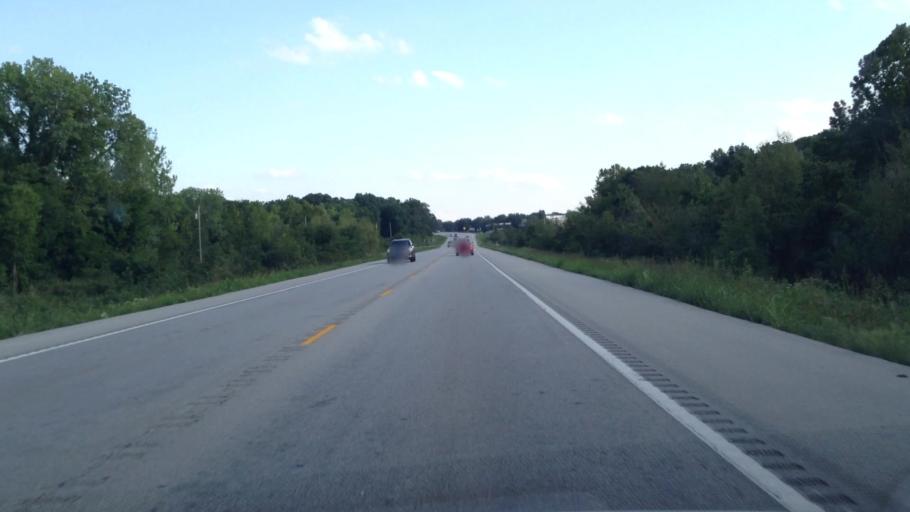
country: US
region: Missouri
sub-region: Jasper County
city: Carl Junction
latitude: 37.1505
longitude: -94.5251
